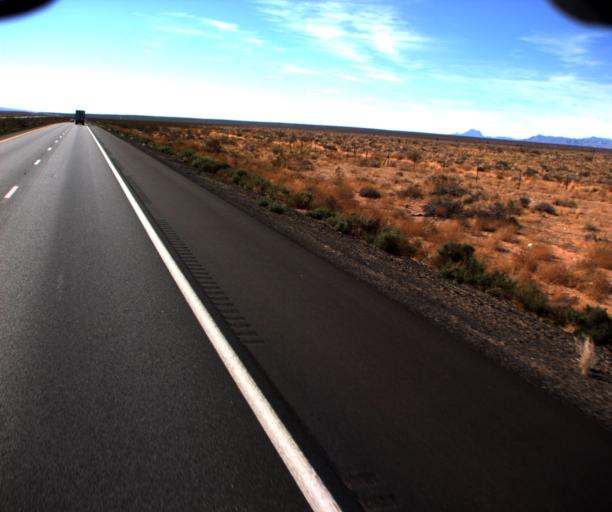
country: US
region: Arizona
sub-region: Mohave County
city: Beaver Dam
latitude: 36.8815
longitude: -113.9461
